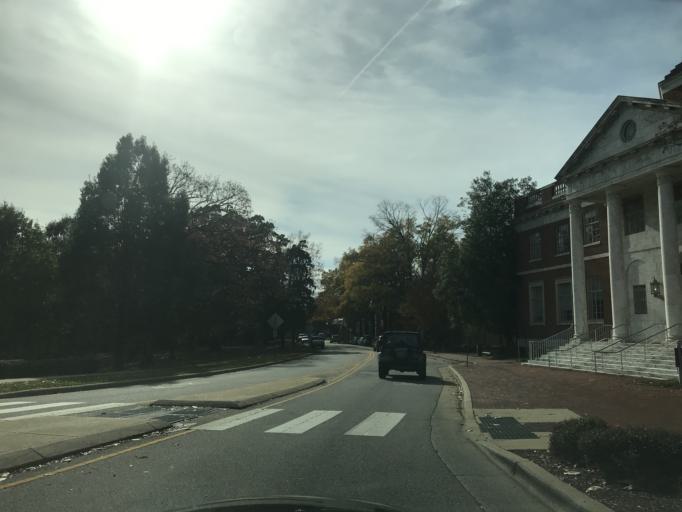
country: US
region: North Carolina
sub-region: Wake County
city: West Raleigh
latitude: 35.7846
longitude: -78.6643
